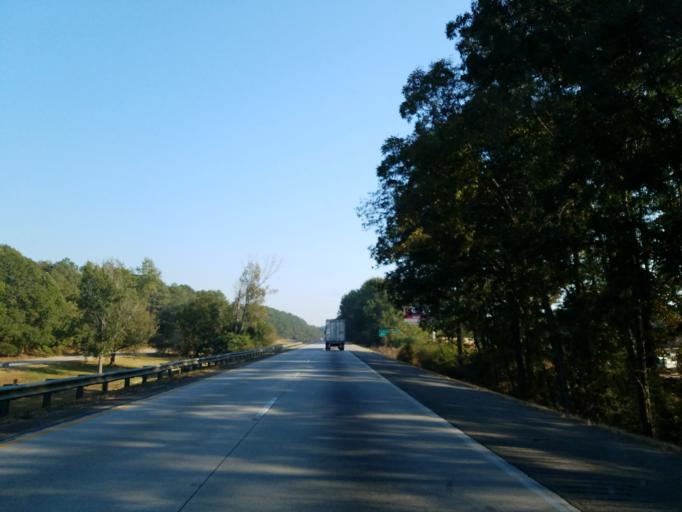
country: US
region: Georgia
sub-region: Monroe County
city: Forsyth
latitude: 32.9549
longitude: -83.8094
